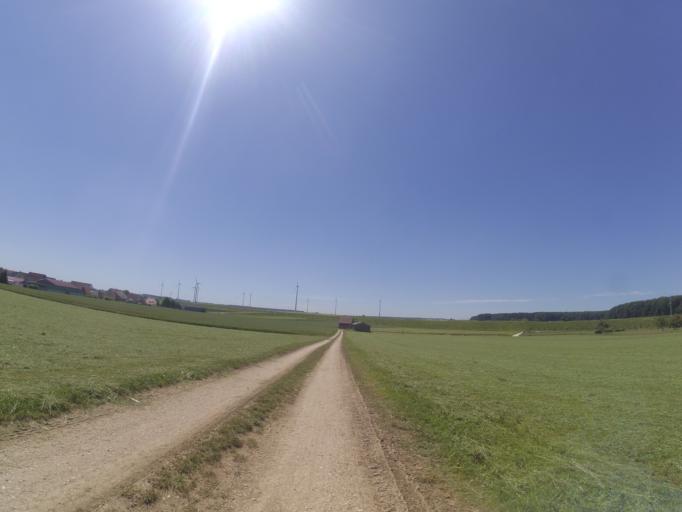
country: DE
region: Baden-Wuerttemberg
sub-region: Tuebingen Region
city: Lonsee
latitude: 48.4911
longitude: 9.8573
